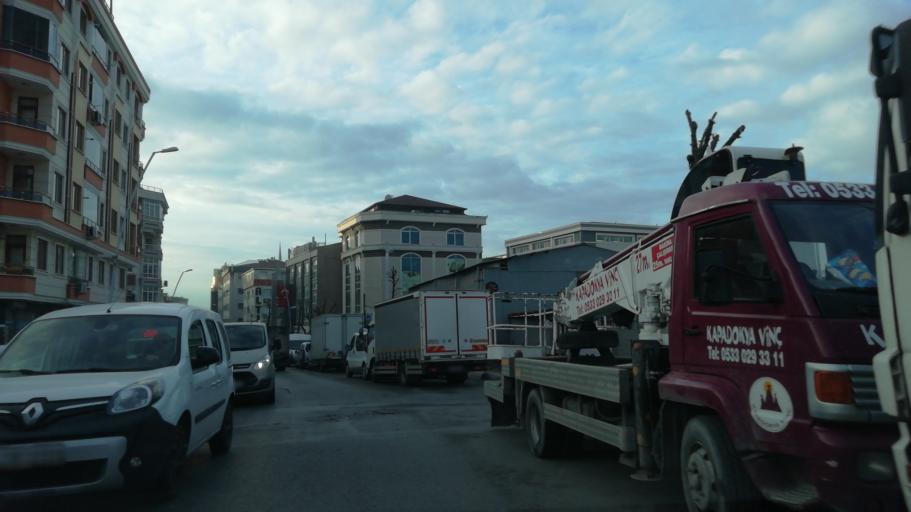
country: TR
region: Istanbul
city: Bahcelievler
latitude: 41.0039
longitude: 28.8265
